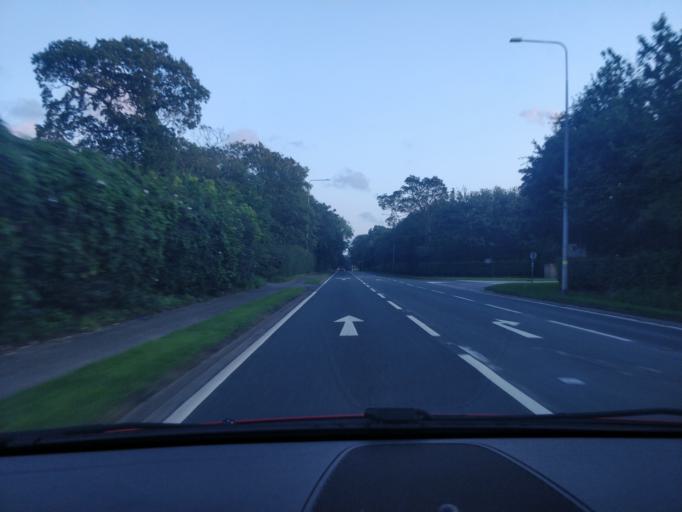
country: GB
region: England
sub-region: Lancashire
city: Tarleton
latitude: 53.6828
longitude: -2.8164
